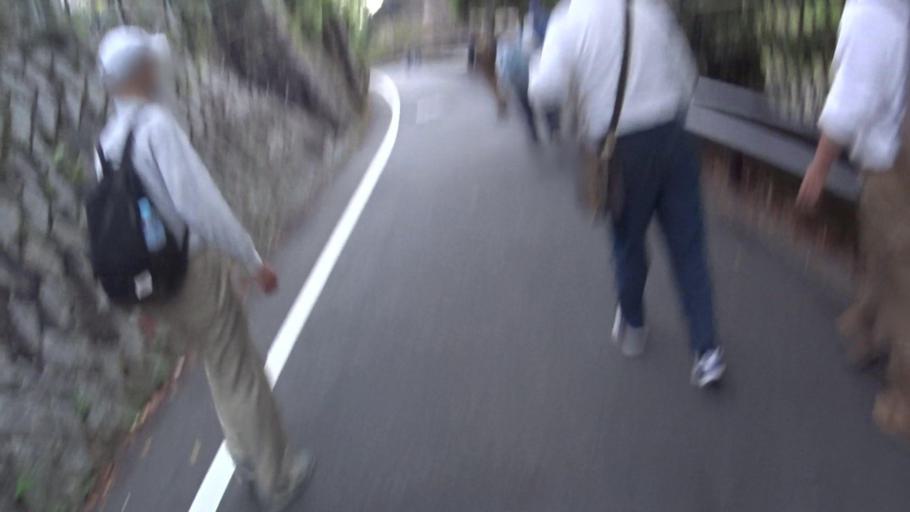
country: JP
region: Osaka
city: Kaizuka
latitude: 34.4518
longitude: 135.2843
